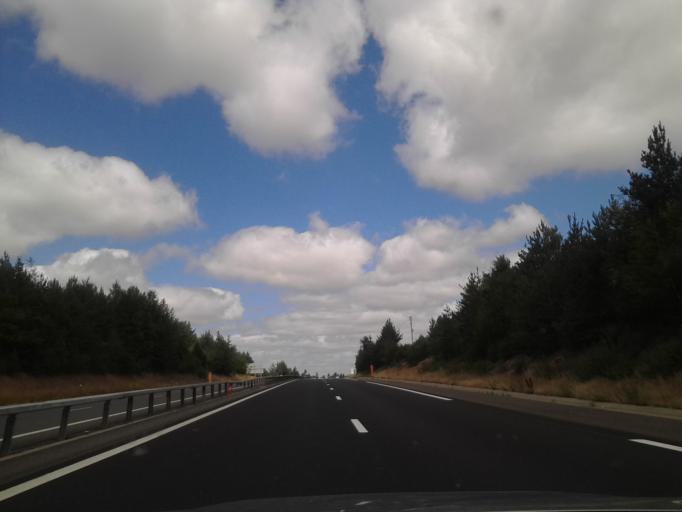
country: FR
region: Languedoc-Roussillon
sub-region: Departement de la Lozere
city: Le Malzieu-Ville
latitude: 44.8581
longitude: 3.2574
